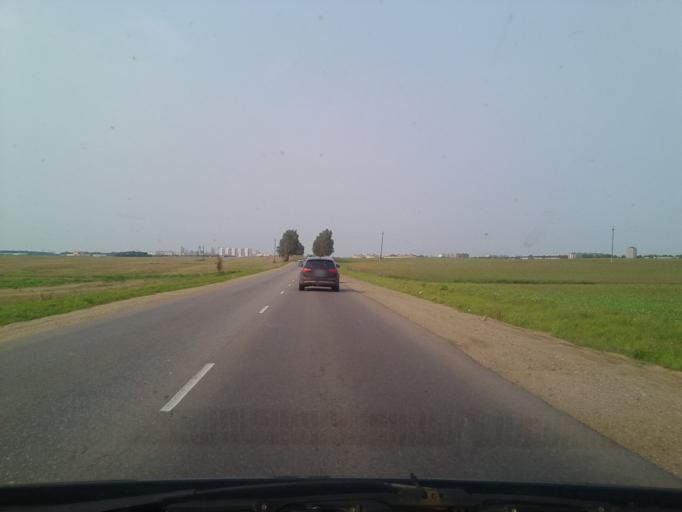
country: BY
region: Minsk
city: Hatava
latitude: 53.8210
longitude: 27.6359
